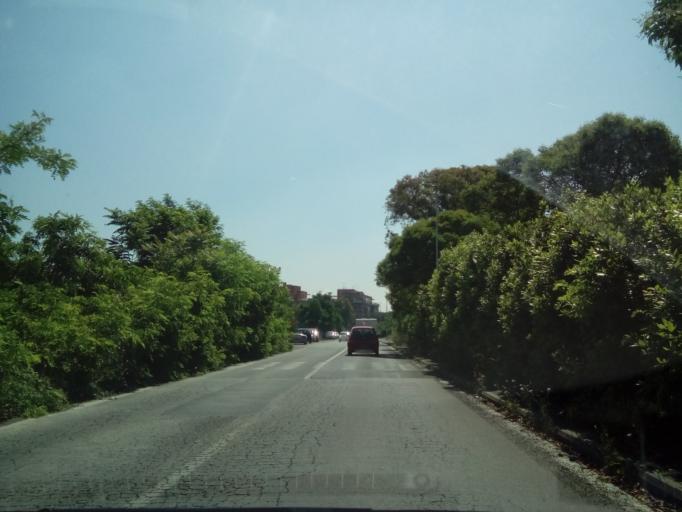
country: IT
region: Latium
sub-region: Citta metropolitana di Roma Capitale
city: Rome
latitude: 41.8920
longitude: 12.5815
